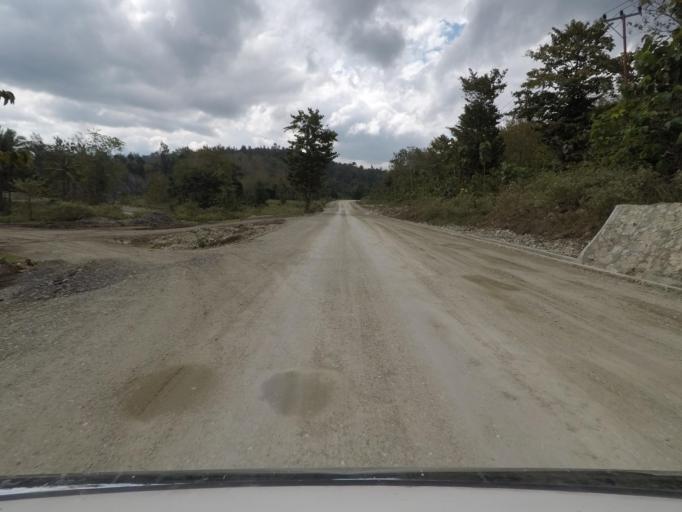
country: TL
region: Viqueque
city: Viqueque
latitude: -8.8207
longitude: 126.3786
